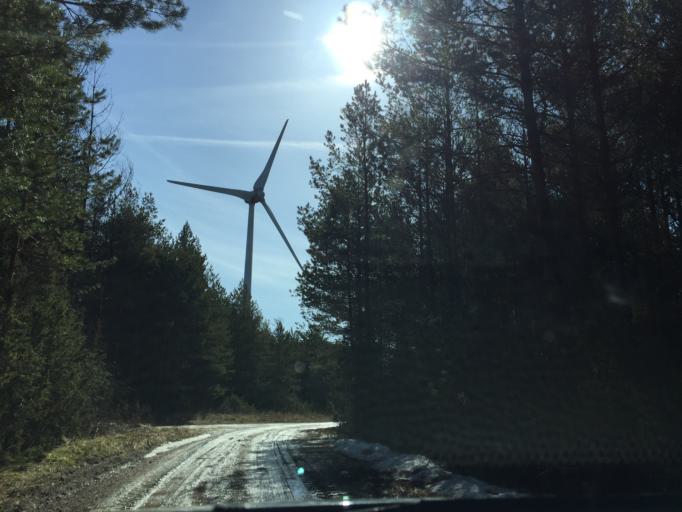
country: EE
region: Laeaene
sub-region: Haapsalu linn
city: Haapsalu
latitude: 58.6384
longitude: 23.5190
